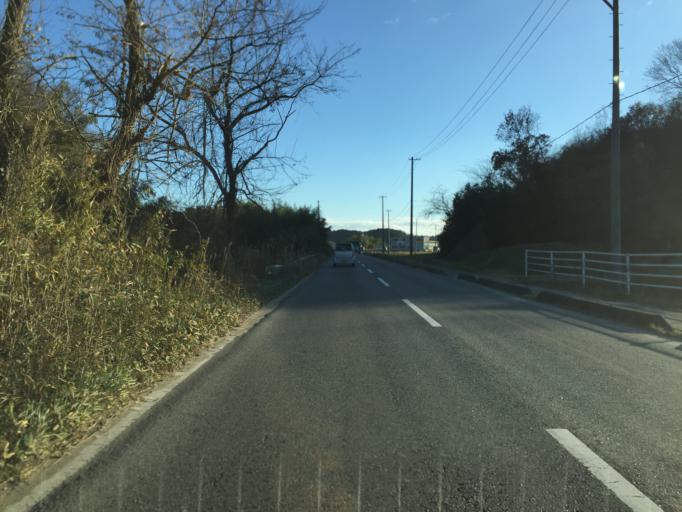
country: JP
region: Fukushima
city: Iwaki
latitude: 37.1115
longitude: 140.8624
